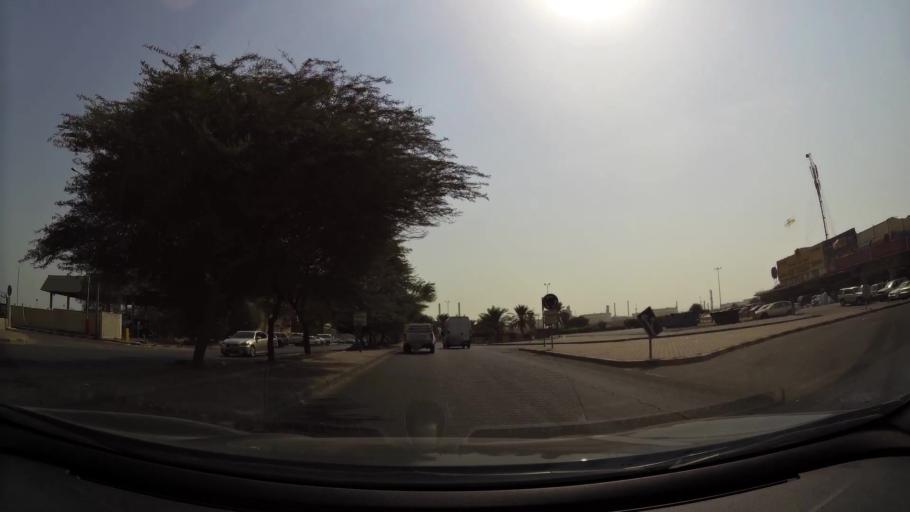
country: KW
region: Al Ahmadi
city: Al Fahahil
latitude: 29.0717
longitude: 48.1258
